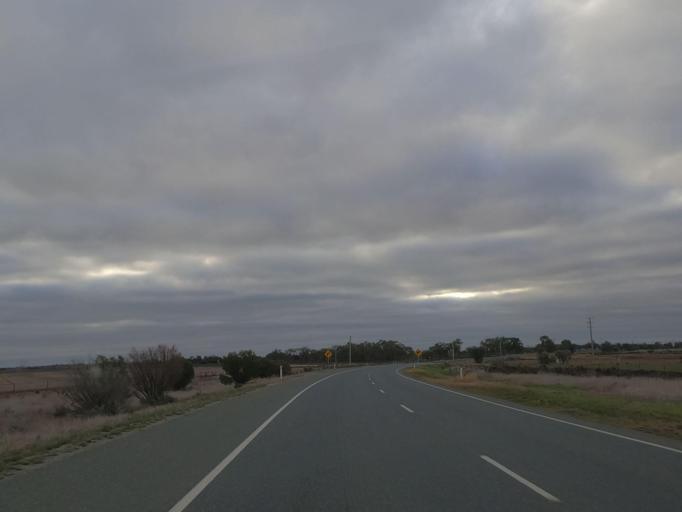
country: AU
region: Victoria
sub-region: Swan Hill
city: Swan Hill
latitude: -35.6240
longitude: 143.8054
